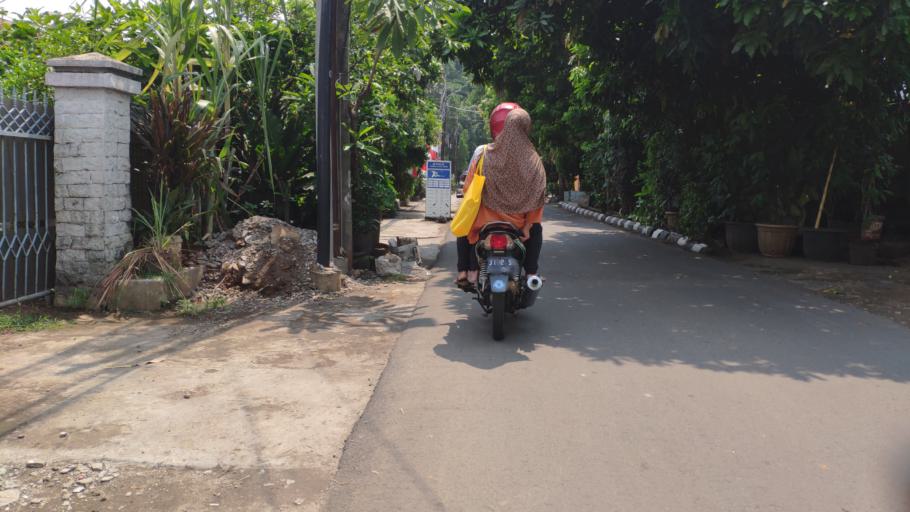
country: ID
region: West Java
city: Pamulang
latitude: -6.3068
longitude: 106.8115
